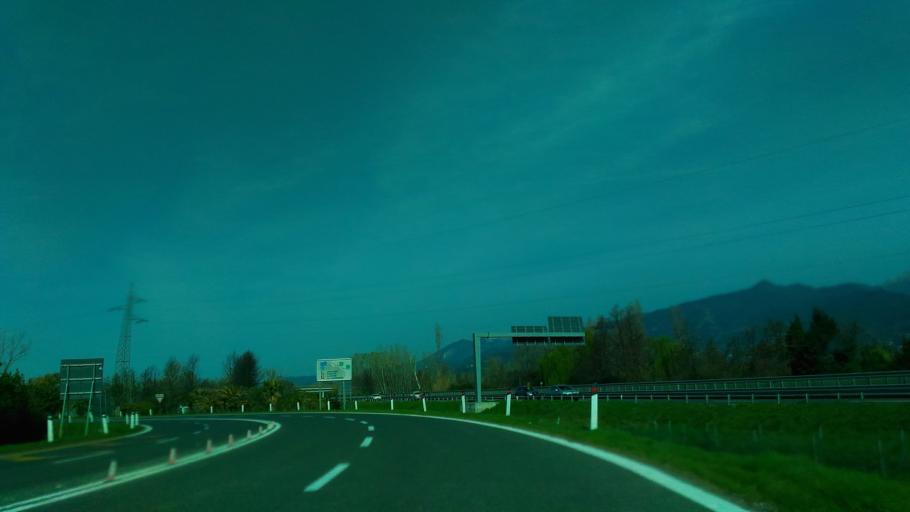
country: IT
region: Tuscany
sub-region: Provincia di Lucca
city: Pietrasanta
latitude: 43.9560
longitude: 10.1995
